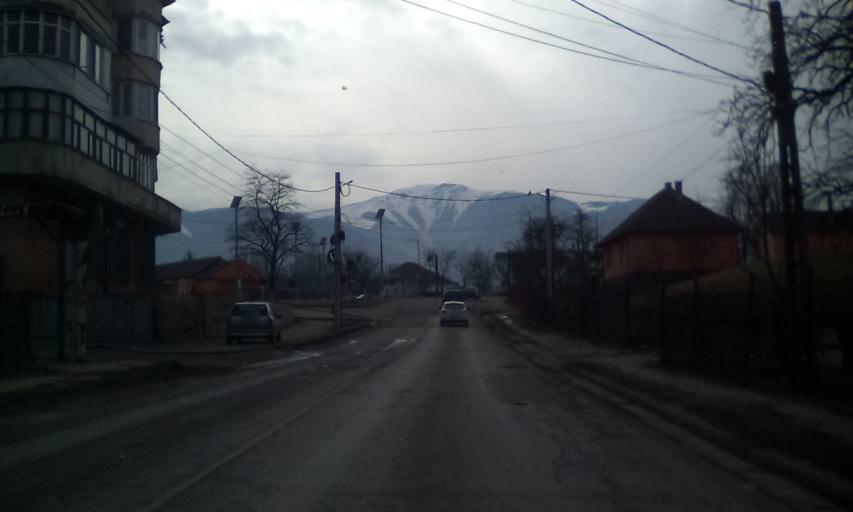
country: RO
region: Hunedoara
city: Vulcan
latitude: 45.3745
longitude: 23.2819
